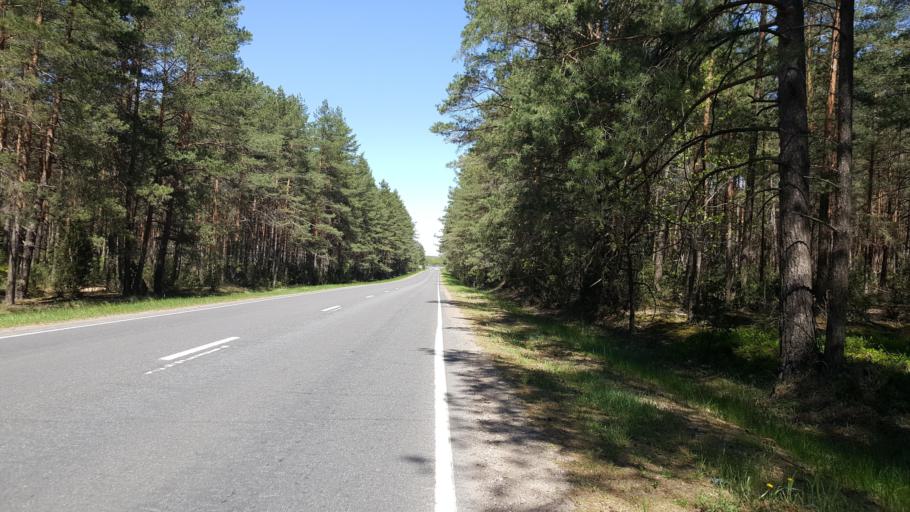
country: BY
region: Brest
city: Kamyanyuki
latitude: 52.5467
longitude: 23.7935
